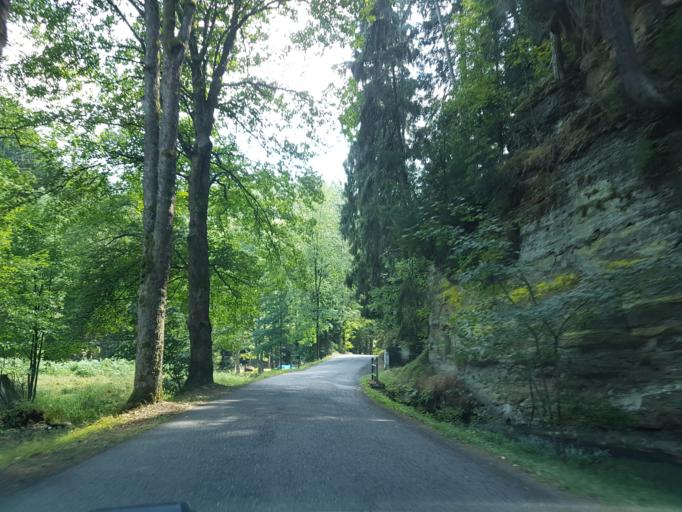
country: CZ
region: Ustecky
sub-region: Okres Decin
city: Chribska
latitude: 50.8580
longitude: 14.4371
